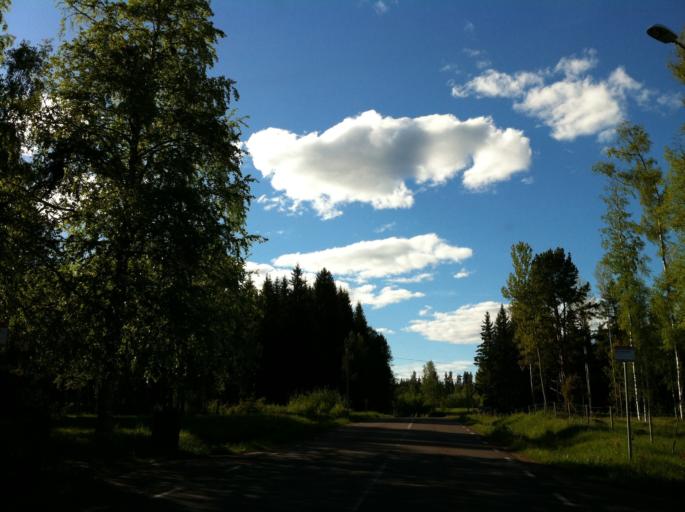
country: SE
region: Dalarna
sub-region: Leksand Municipality
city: Leksand
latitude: 60.7381
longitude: 14.9429
